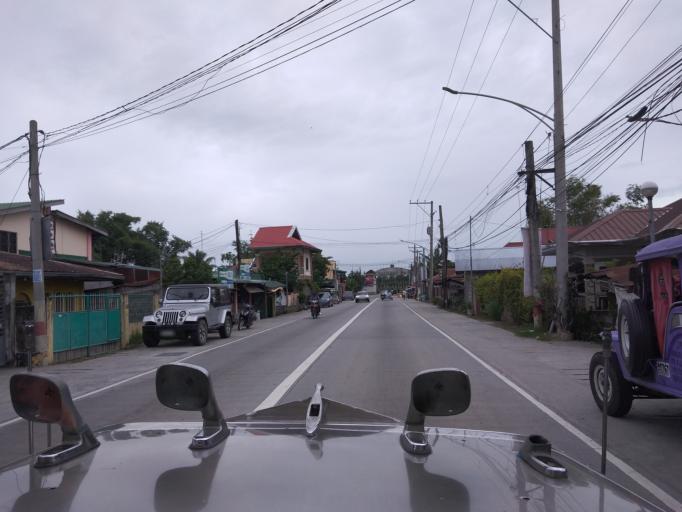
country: PH
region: Central Luzon
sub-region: Province of Pampanga
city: Pandacaqui
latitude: 15.1895
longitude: 120.6352
